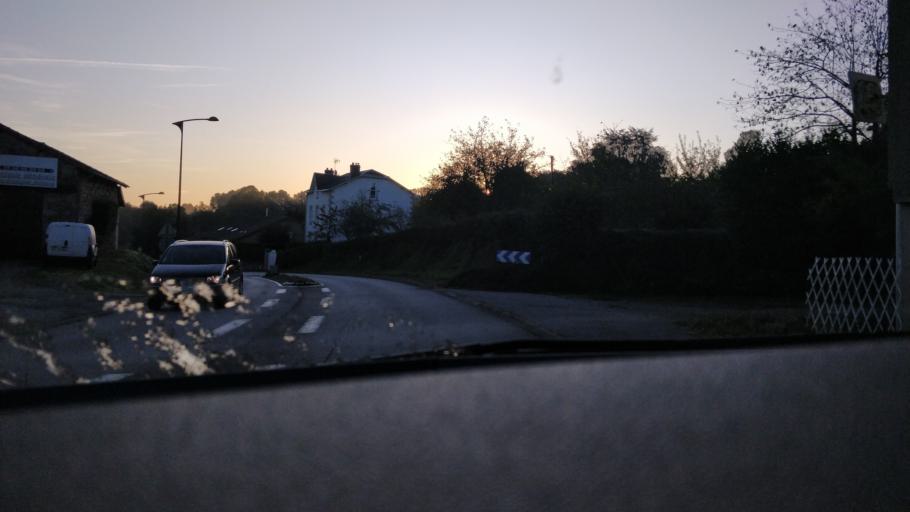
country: FR
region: Limousin
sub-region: Departement de la Haute-Vienne
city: Saint-Just-le-Martel
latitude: 45.8455
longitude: 1.3777
